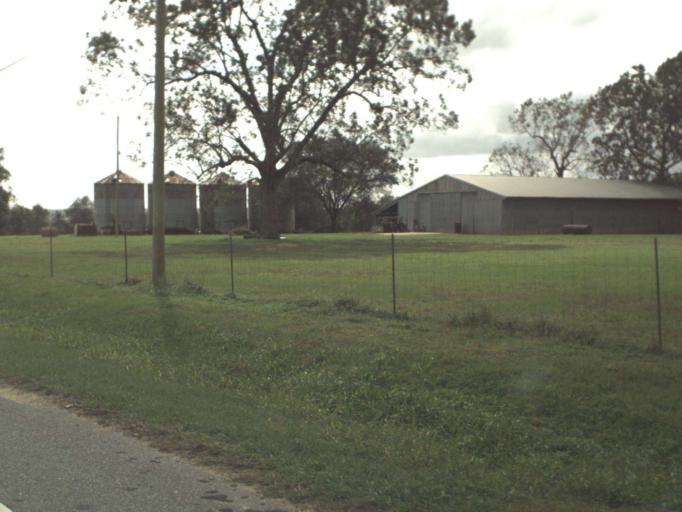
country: US
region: Florida
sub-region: Santa Rosa County
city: Point Baker
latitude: 30.8331
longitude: -87.0488
